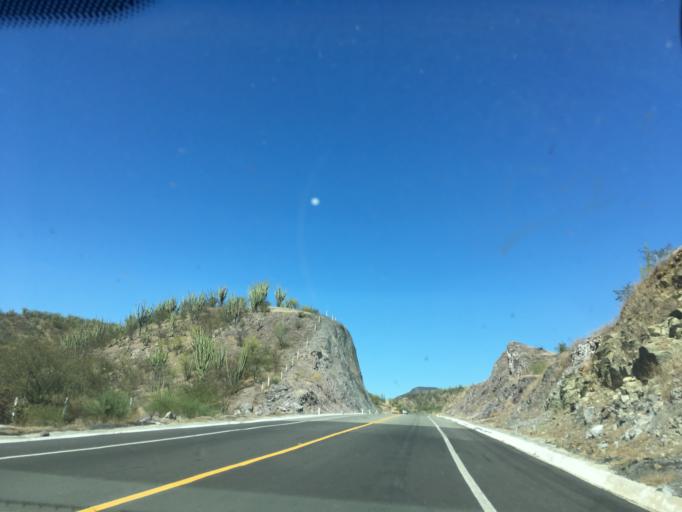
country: MX
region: Michoacan
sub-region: Arteaga
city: Infiernillo (Morelos de Infiernillo)
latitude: 18.2980
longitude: -101.9057
